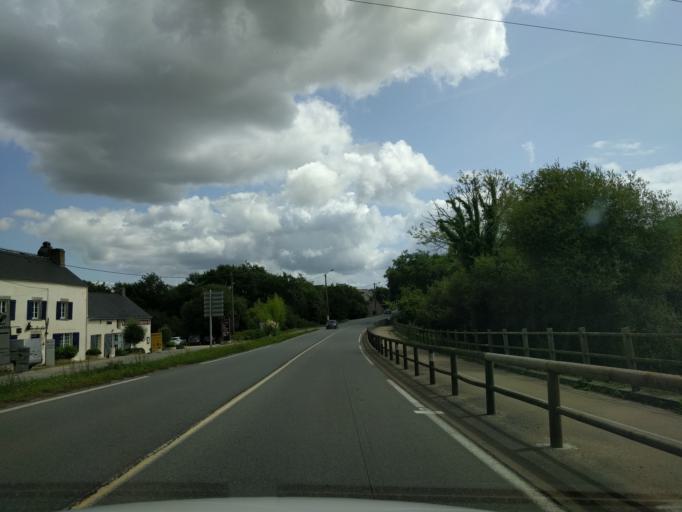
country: FR
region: Brittany
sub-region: Departement du Morbihan
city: Sene
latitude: 47.6492
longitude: -2.7118
